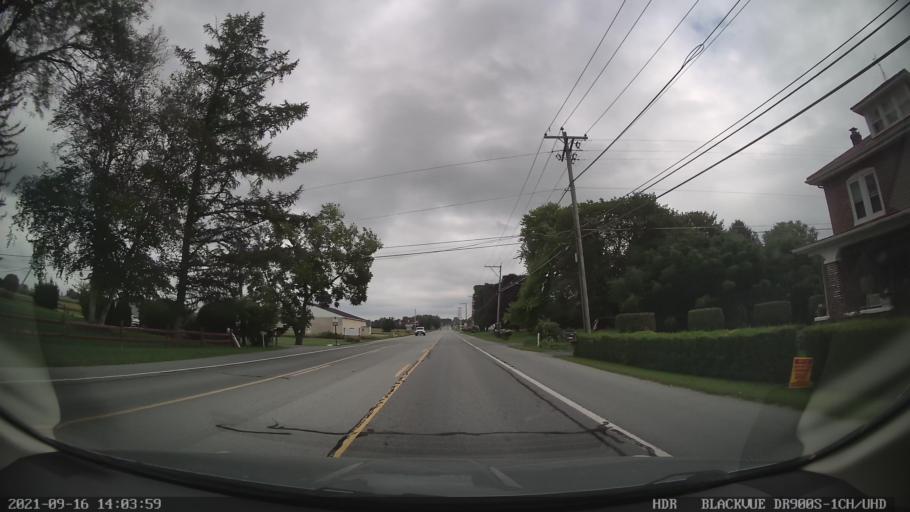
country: US
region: Pennsylvania
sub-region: Berks County
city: Kutztown
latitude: 40.5004
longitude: -75.7989
